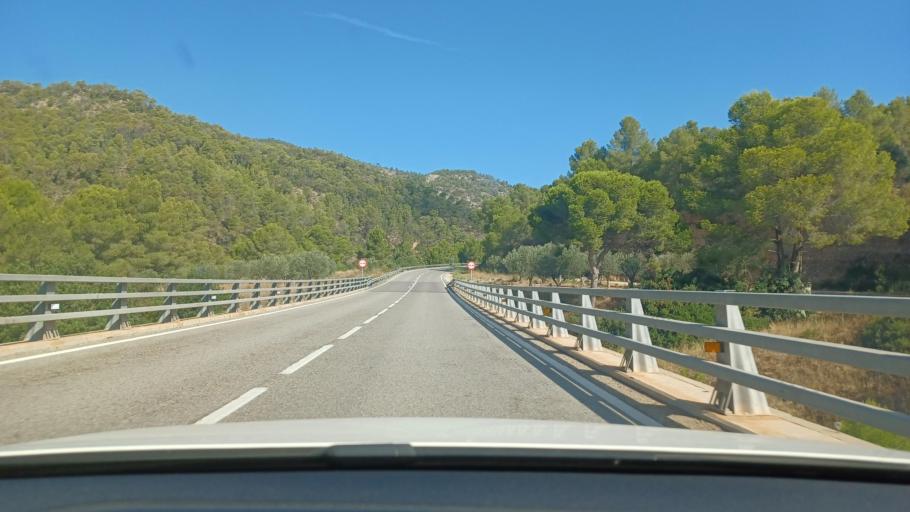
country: ES
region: Catalonia
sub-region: Provincia de Tarragona
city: Benifallet
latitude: 40.9527
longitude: 0.4477
